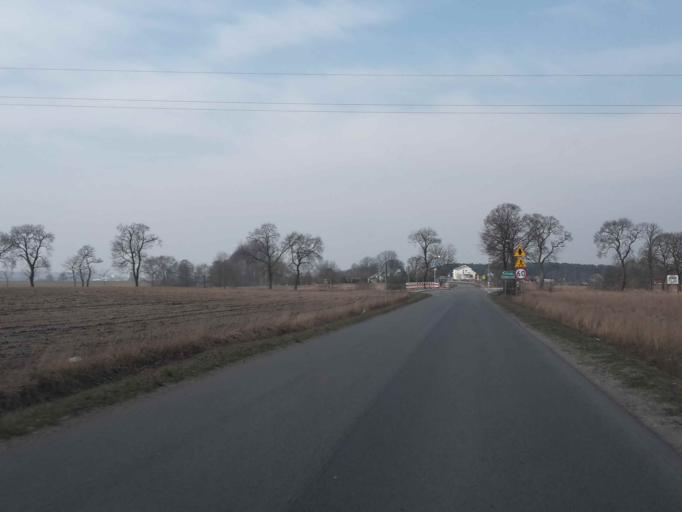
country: PL
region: Kujawsko-Pomorskie
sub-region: Powiat nakielski
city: Szubin
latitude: 53.0830
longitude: 17.7754
